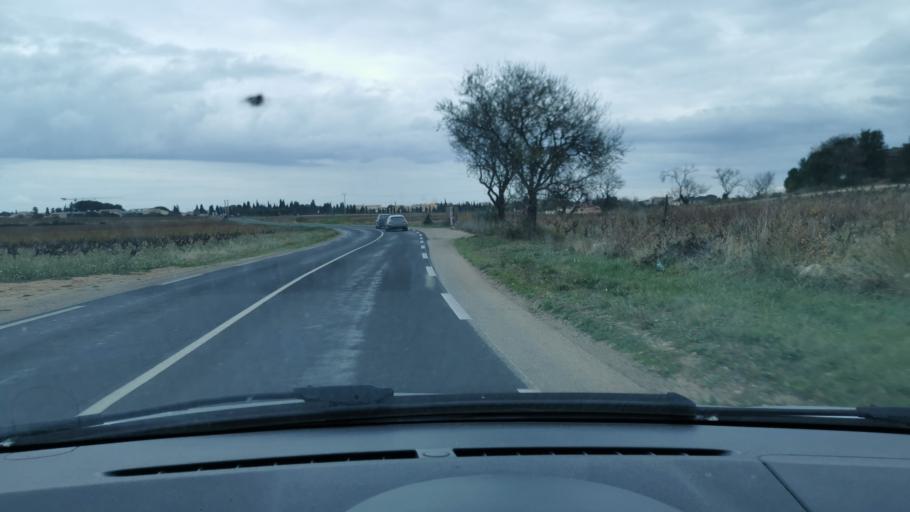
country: FR
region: Languedoc-Roussillon
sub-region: Departement de l'Herault
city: Frontignan
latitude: 43.4480
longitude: 3.7340
